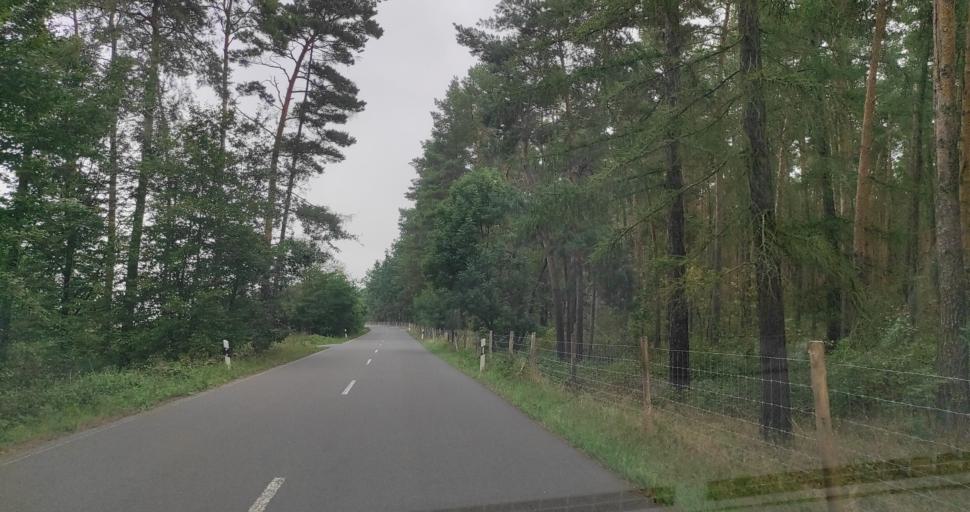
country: DE
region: Brandenburg
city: Forst
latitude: 51.7175
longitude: 14.5445
